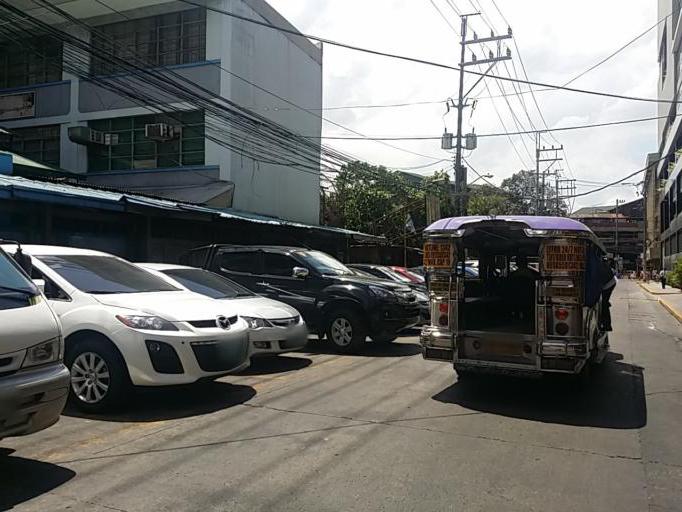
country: PH
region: Metro Manila
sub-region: City of Manila
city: Manila
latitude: 14.6046
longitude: 120.9884
